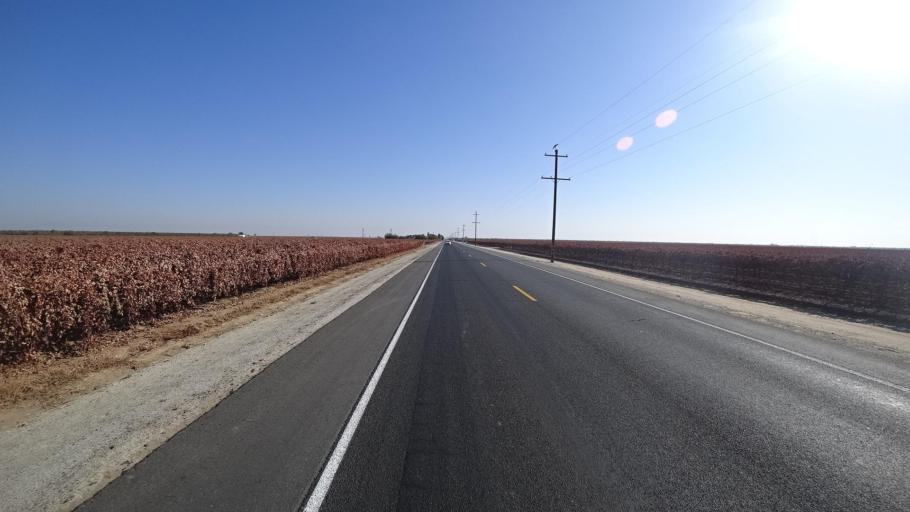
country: US
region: California
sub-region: Kern County
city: McFarland
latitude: 35.7177
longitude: -119.2666
